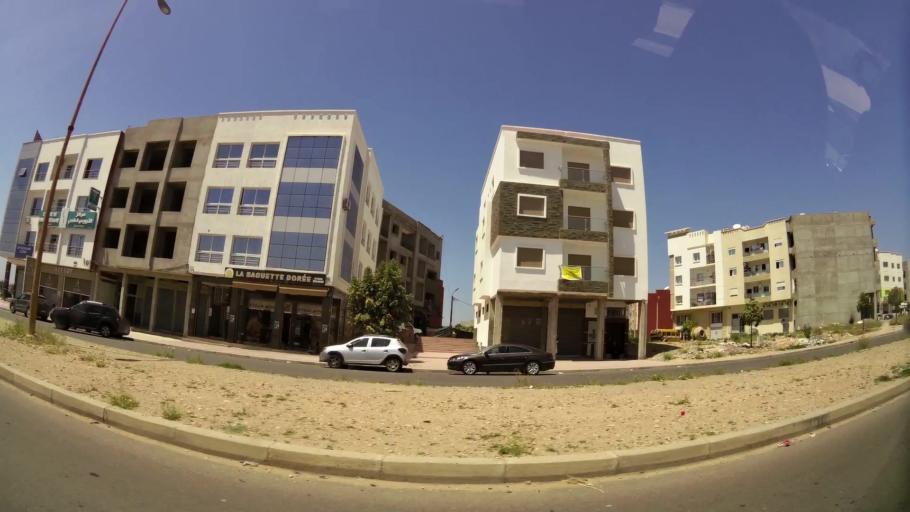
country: MA
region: Oued ed Dahab-Lagouira
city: Dakhla
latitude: 30.4275
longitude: -9.5563
